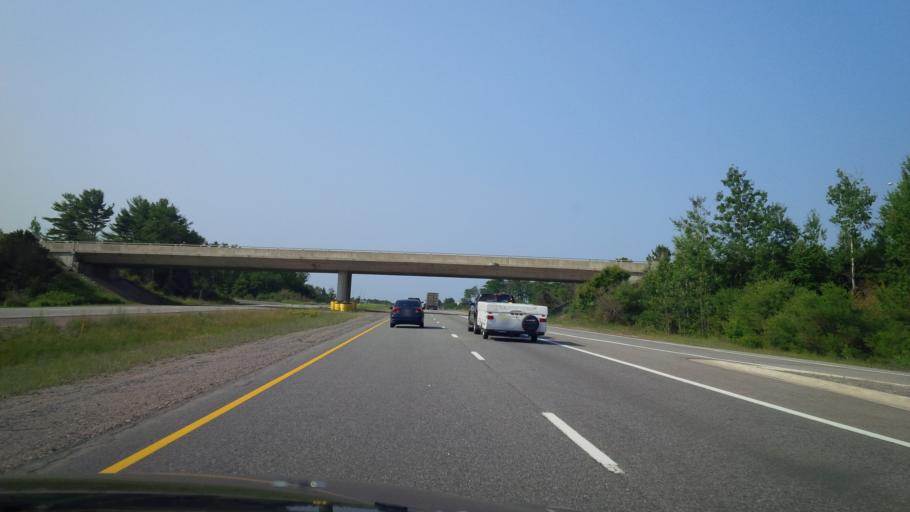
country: CA
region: Ontario
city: Bracebridge
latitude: 44.9964
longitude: -79.3058
